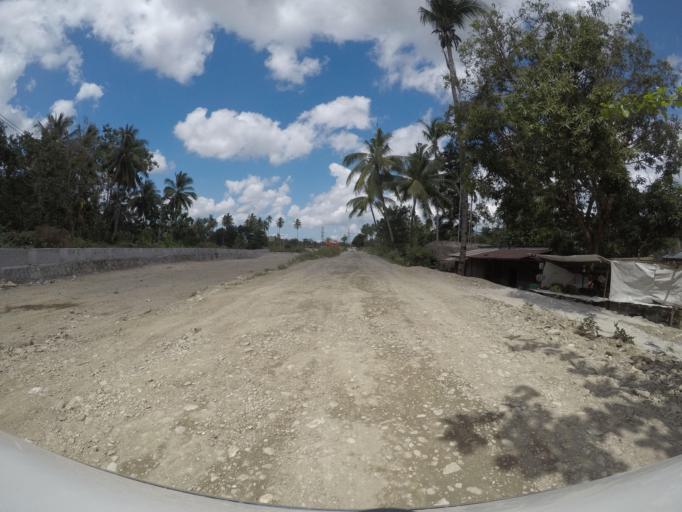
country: TL
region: Viqueque
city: Viqueque
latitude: -8.8334
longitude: 126.3731
